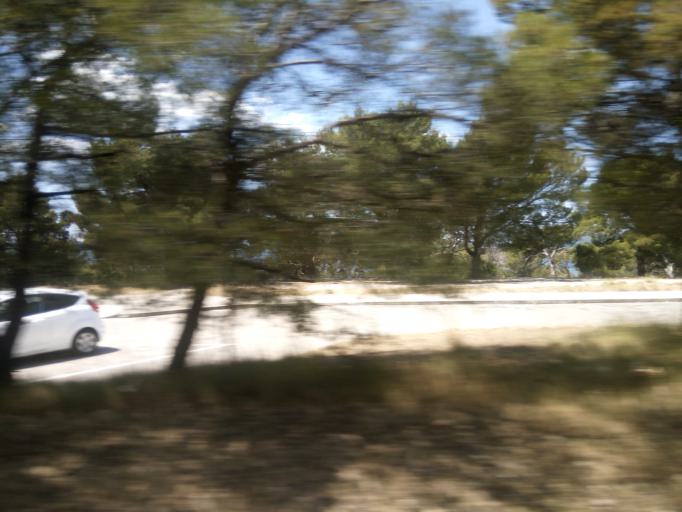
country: HR
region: Sibensko-Kniniska
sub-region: Grad Sibenik
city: Brodarica
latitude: 43.6716
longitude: 15.9302
